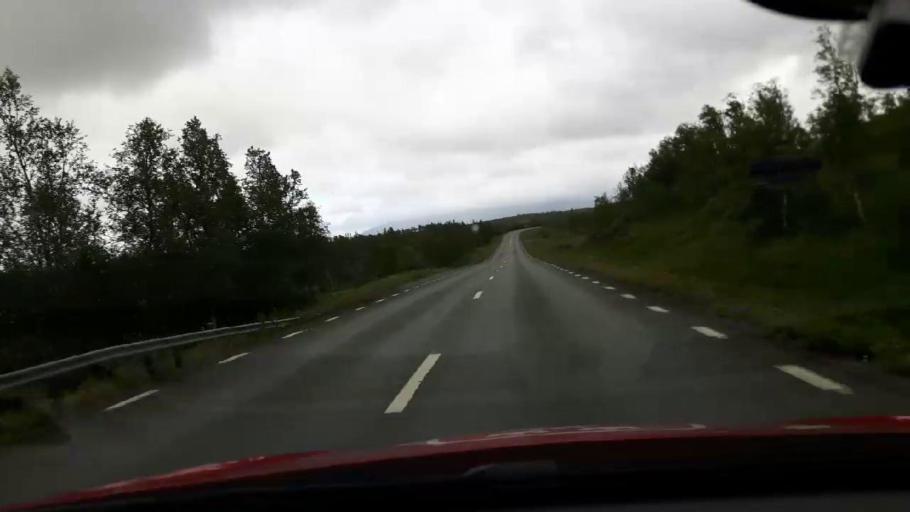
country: NO
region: Nord-Trondelag
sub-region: Meraker
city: Meraker
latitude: 63.3143
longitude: 12.0992
